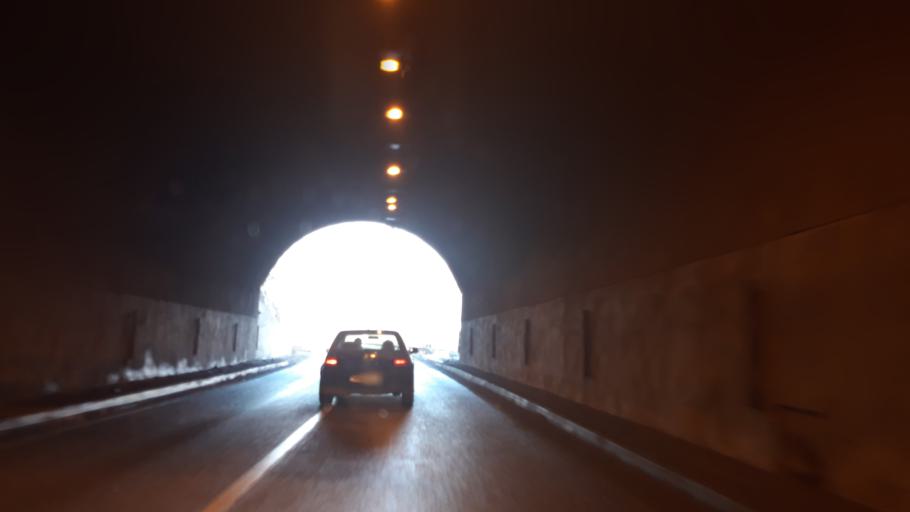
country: BA
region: Republika Srpska
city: Pale
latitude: 43.8407
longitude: 18.4928
